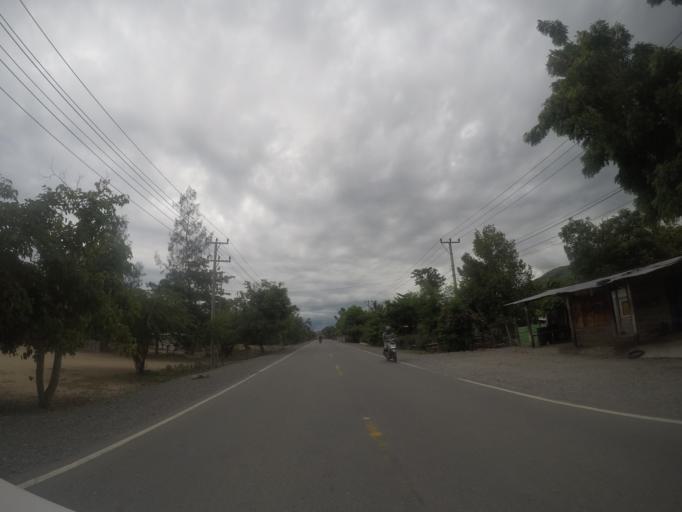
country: TL
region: Liquica
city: Liquica
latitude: -8.5653
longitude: 125.4194
